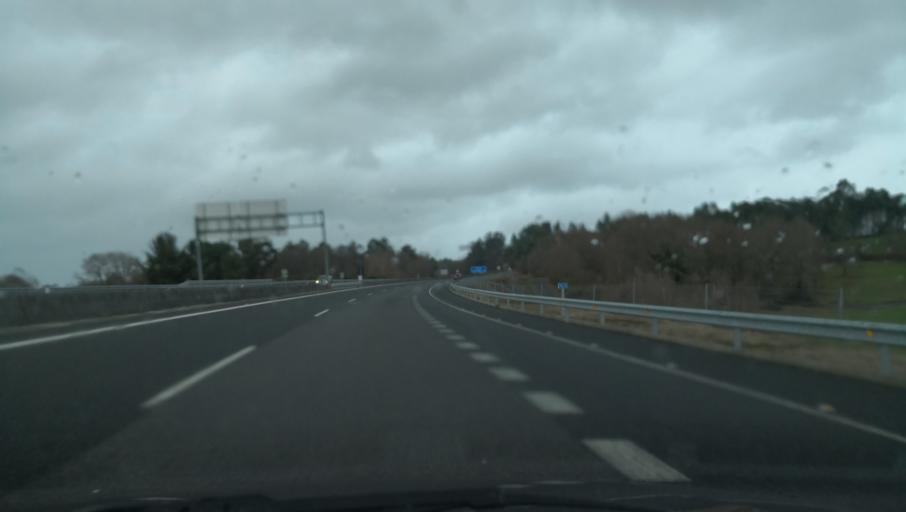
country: ES
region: Galicia
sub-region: Provincia de Pontevedra
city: Lalin
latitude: 42.6766
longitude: -8.1622
